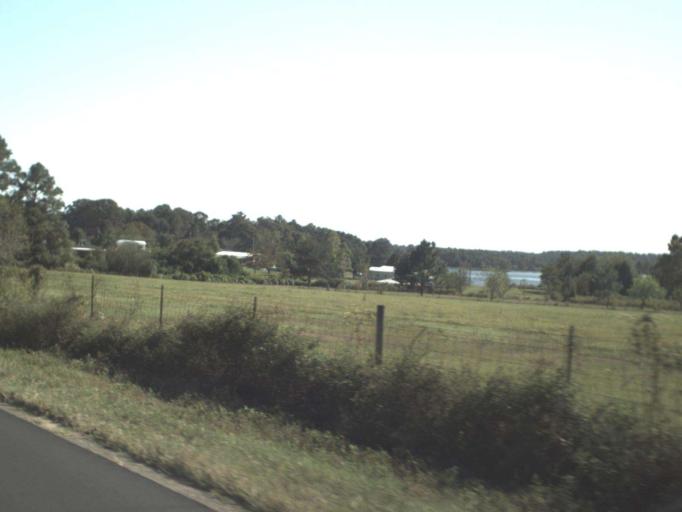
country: US
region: Florida
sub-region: Walton County
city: DeFuniak Springs
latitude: 30.7926
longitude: -86.1871
